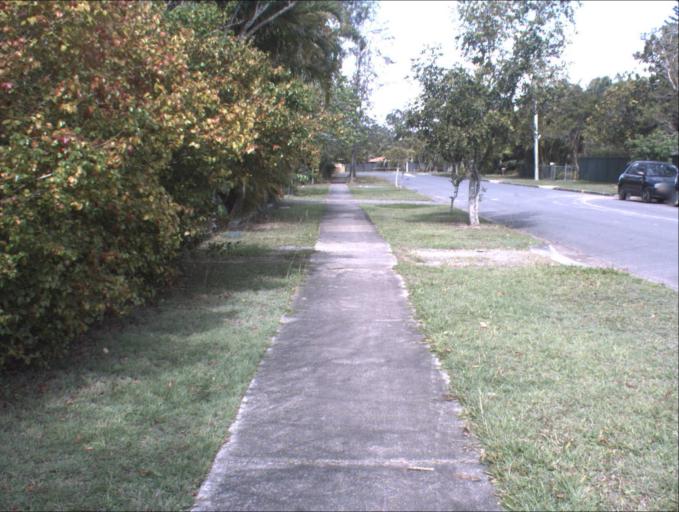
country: AU
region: Queensland
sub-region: Logan
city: Waterford West
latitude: -27.6771
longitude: 153.1099
